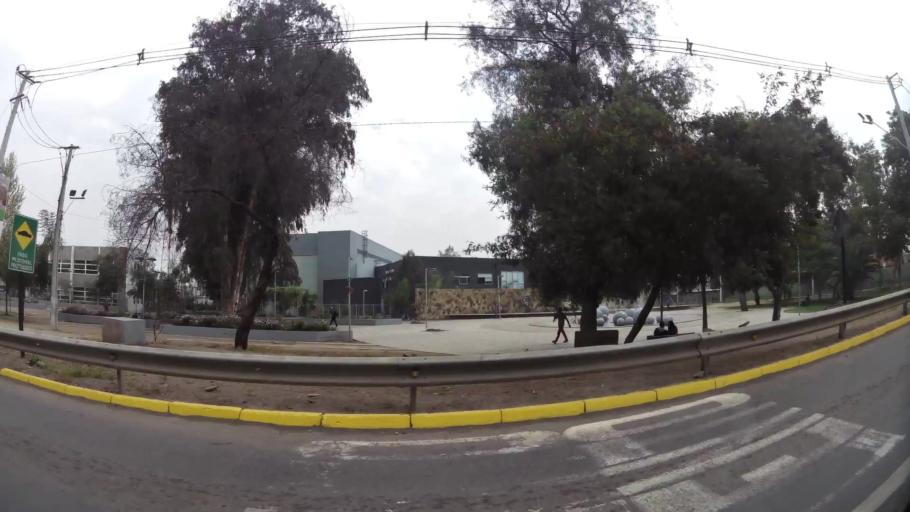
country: CL
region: Santiago Metropolitan
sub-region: Provincia de Chacabuco
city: Chicureo Abajo
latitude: -33.2044
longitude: -70.6830
